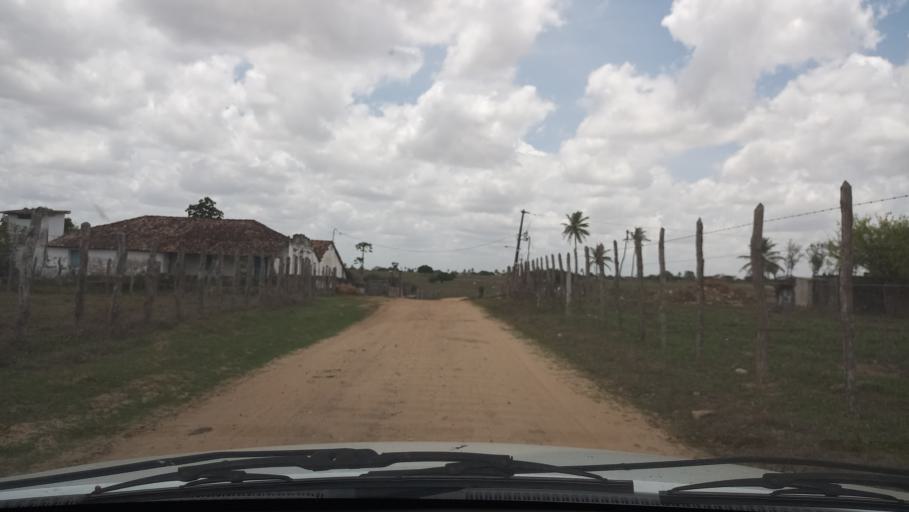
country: BR
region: Rio Grande do Norte
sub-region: Brejinho
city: Brejinho
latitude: -6.2738
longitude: -35.3378
